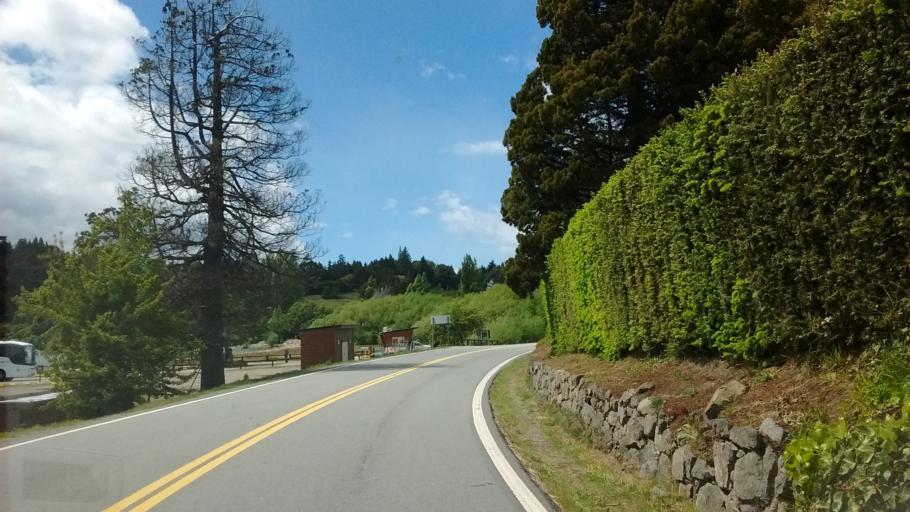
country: AR
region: Rio Negro
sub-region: Departamento de Bariloche
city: San Carlos de Bariloche
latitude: -41.0540
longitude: -71.5328
